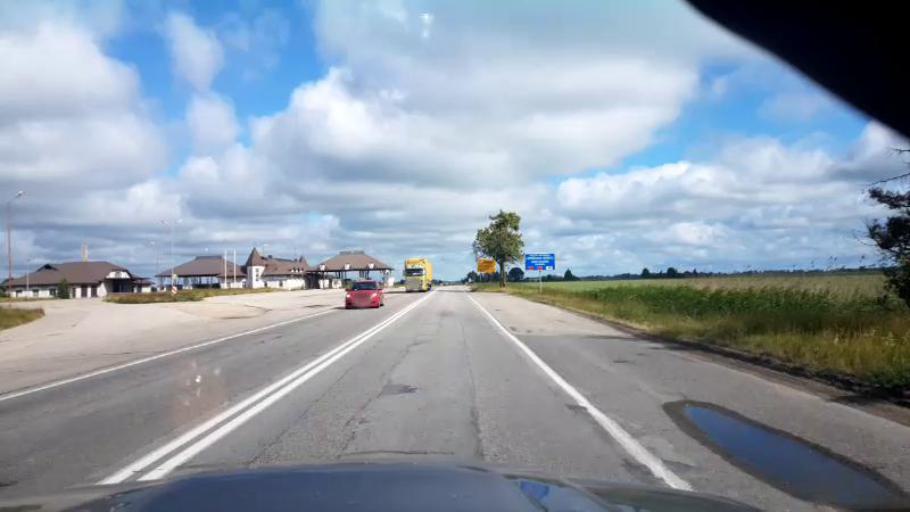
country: LV
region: Bauskas Rajons
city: Bauska
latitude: 56.2772
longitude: 24.3637
